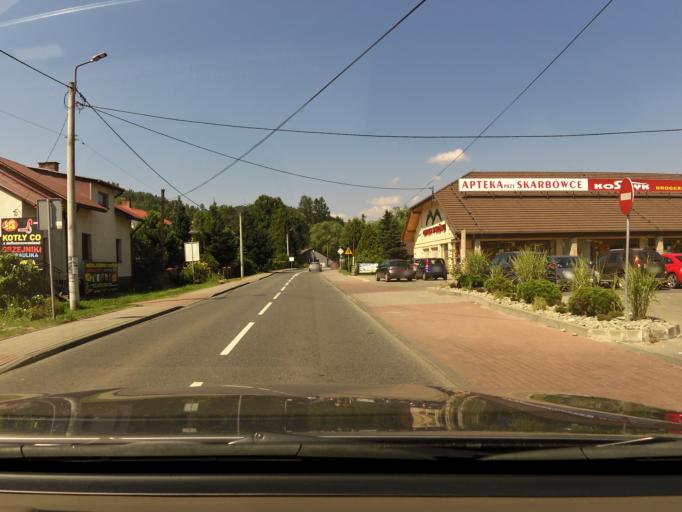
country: PL
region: Silesian Voivodeship
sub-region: Powiat zywiecki
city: Milowka
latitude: 49.5592
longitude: 19.0841
